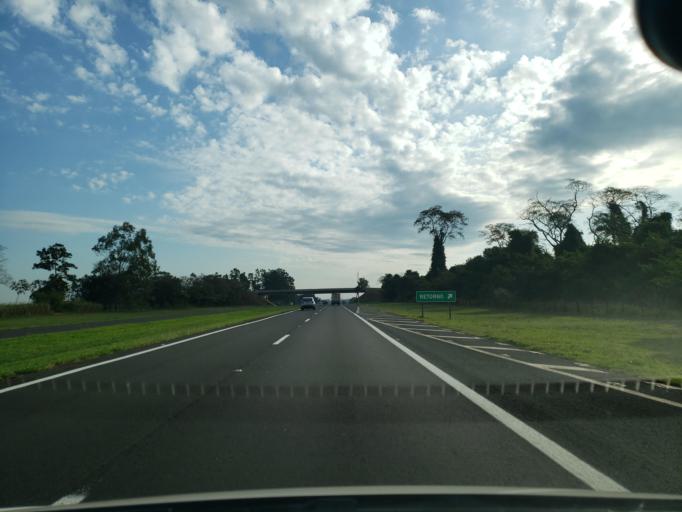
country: BR
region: Sao Paulo
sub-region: Guararapes
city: Guararapes
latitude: -21.2040
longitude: -50.6138
